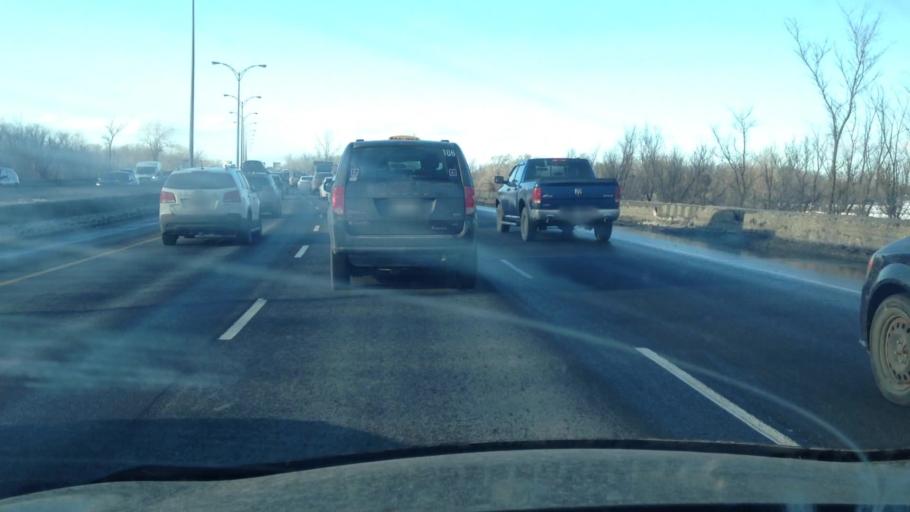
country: CA
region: Quebec
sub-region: Laurentides
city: Boisbriand
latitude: 45.6064
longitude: -73.8071
